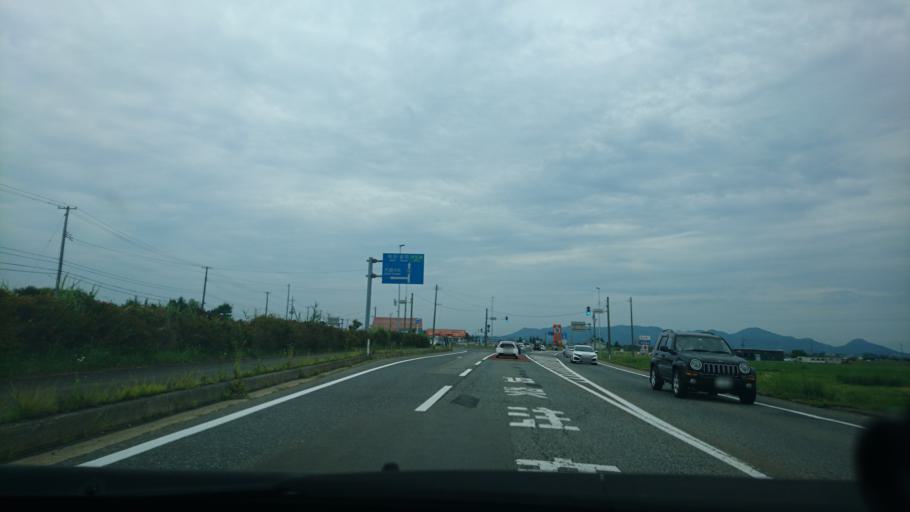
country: JP
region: Akita
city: Omagari
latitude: 39.4218
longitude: 140.5222
